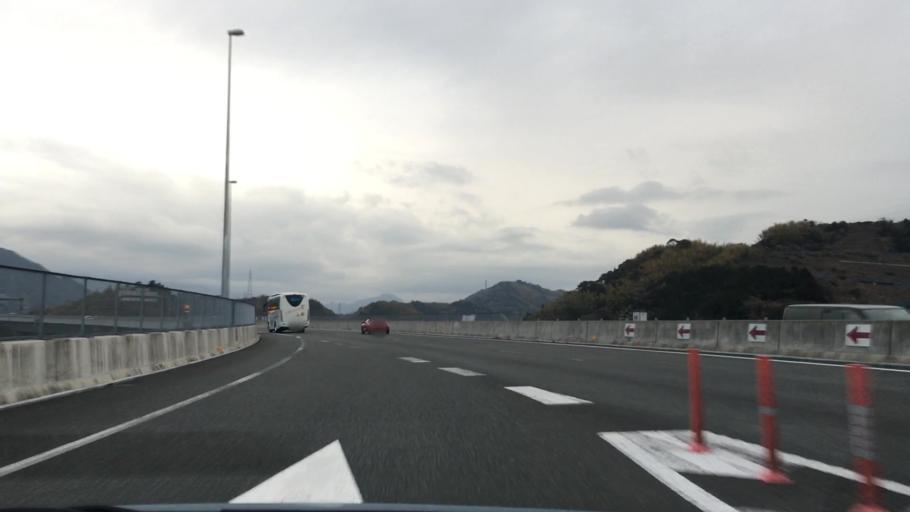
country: JP
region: Shizuoka
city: Shizuoka-shi
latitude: 35.0495
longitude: 138.4874
